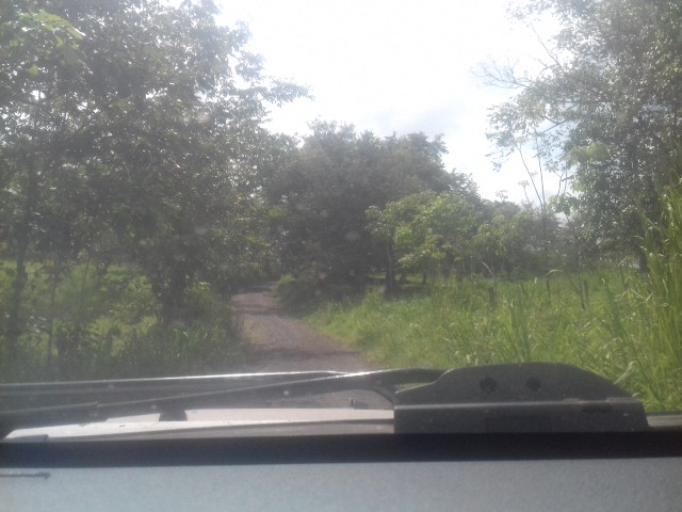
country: NI
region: Jinotega
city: San Jose de Bocay
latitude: 13.5034
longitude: -85.2363
